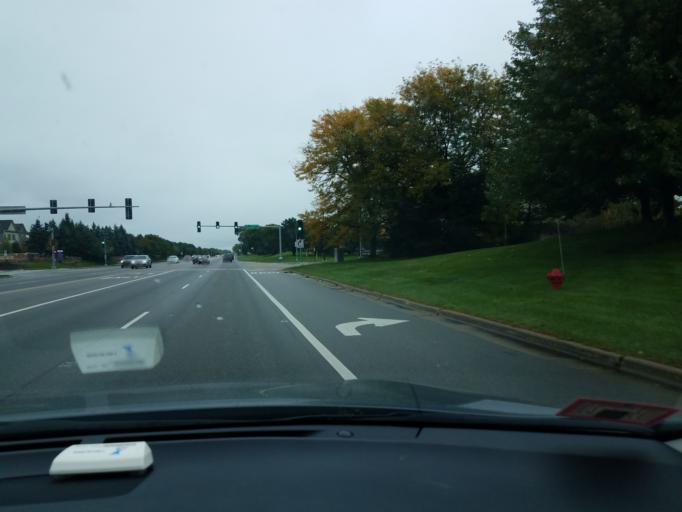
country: US
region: Illinois
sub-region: Lake County
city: Lincolnshire
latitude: 42.1891
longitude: -87.9289
